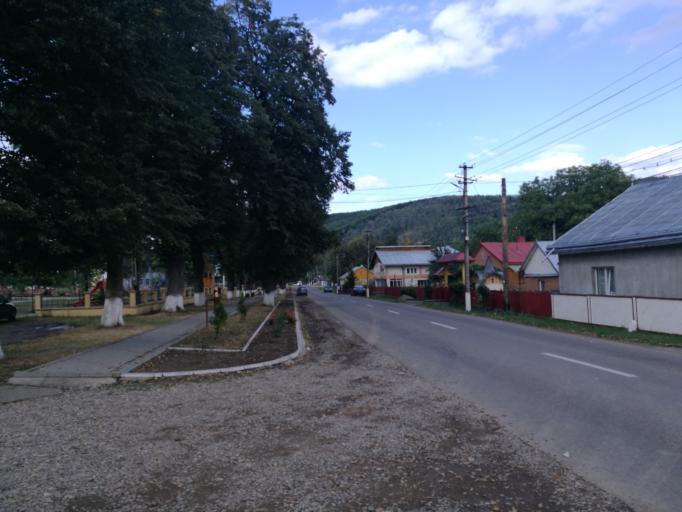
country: RO
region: Suceava
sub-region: Comuna Patrauti
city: Patrauti
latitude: 47.7161
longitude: 26.1900
